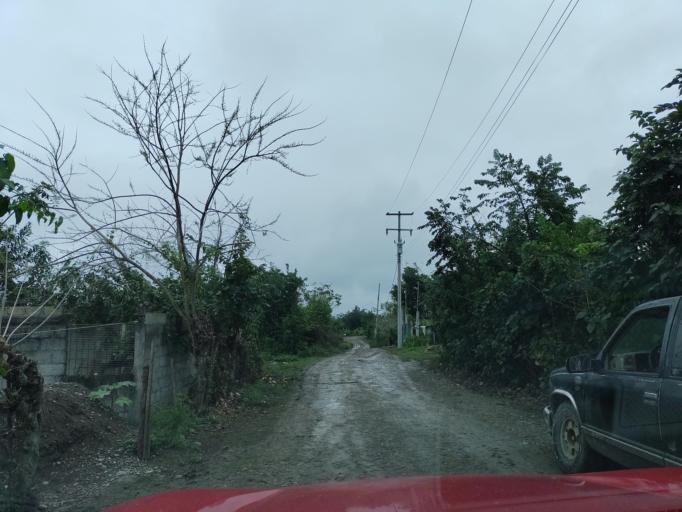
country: MX
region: Veracruz
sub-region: Papantla
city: El Chote
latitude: 20.3947
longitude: -97.3967
